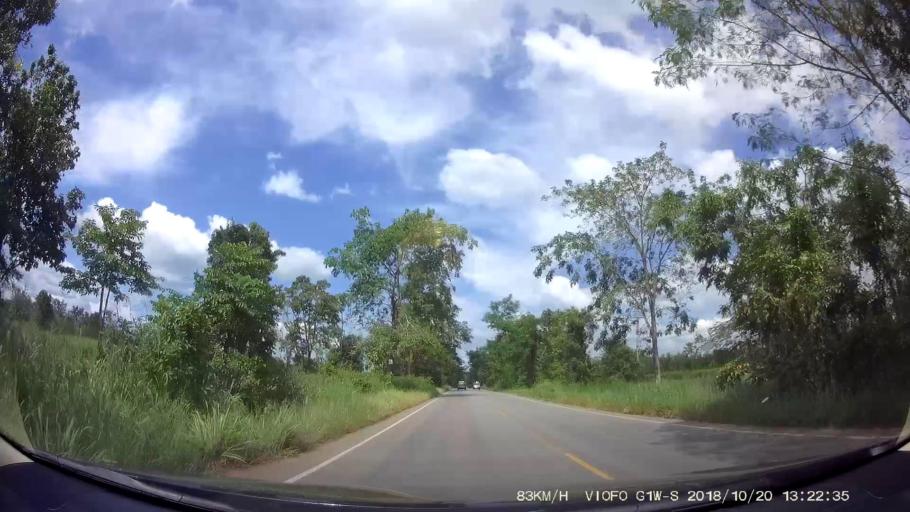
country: TH
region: Chaiyaphum
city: Khon San
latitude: 16.5735
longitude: 101.9166
